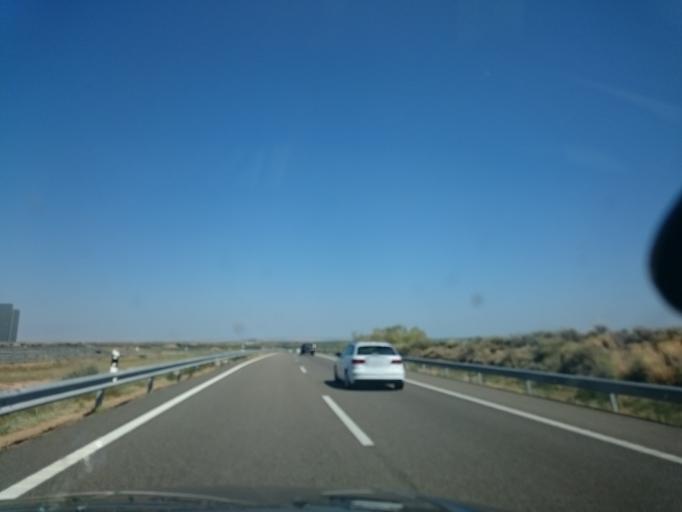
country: ES
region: Aragon
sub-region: Provincia de Huesca
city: Penalba
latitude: 41.5120
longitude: 0.0129
